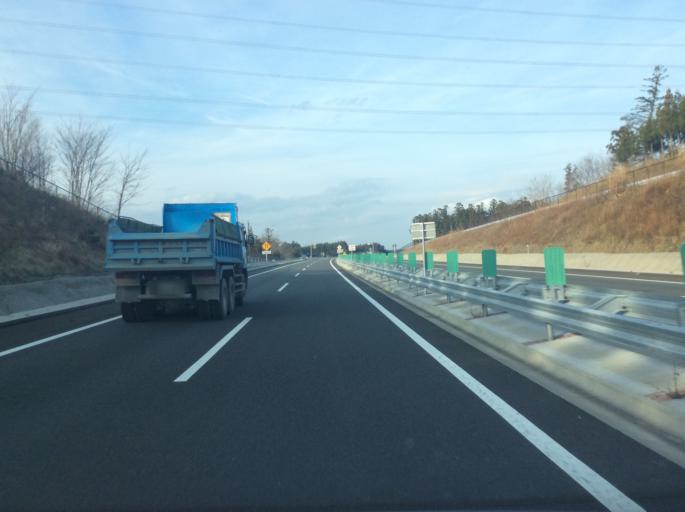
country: JP
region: Fukushima
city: Namie
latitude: 37.5285
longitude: 140.9421
